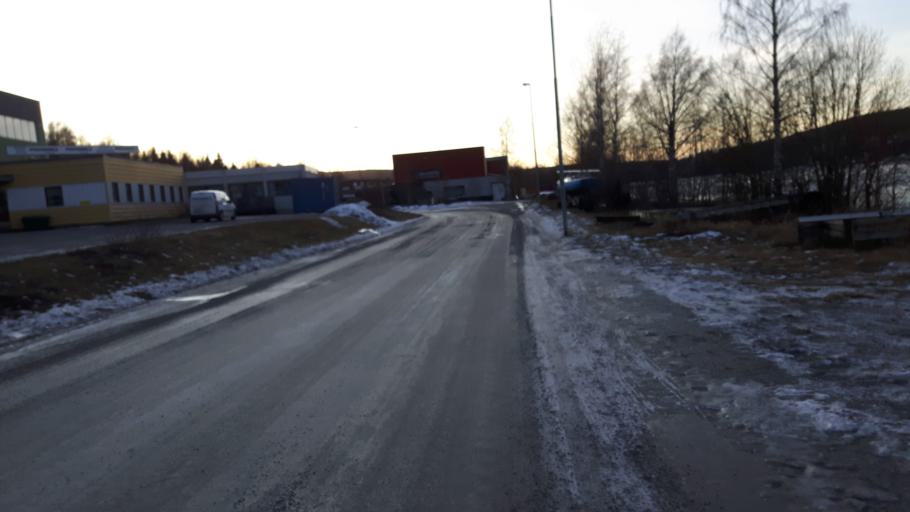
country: SE
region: Vaesternorrland
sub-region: Haernoesands Kommun
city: Haernoesand
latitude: 62.6230
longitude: 17.9450
